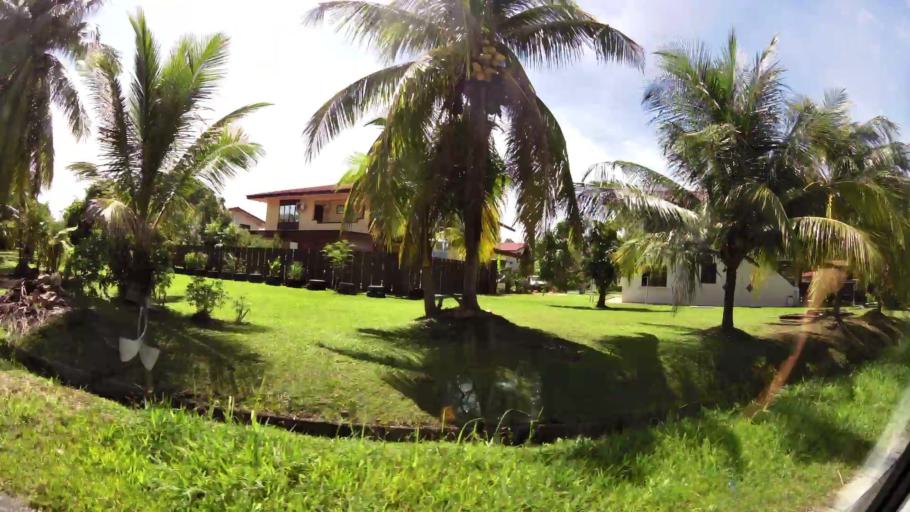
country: BN
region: Belait
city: Kuala Belait
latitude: 4.5843
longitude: 114.2208
